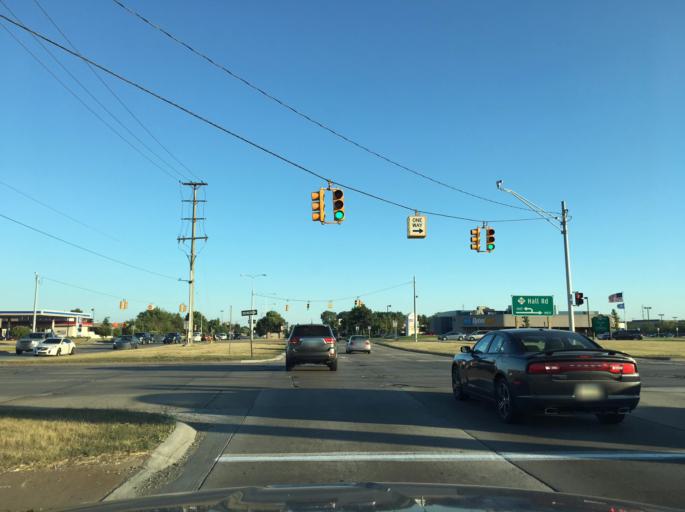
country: US
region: Michigan
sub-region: Macomb County
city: Utica
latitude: 42.6276
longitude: -82.9933
